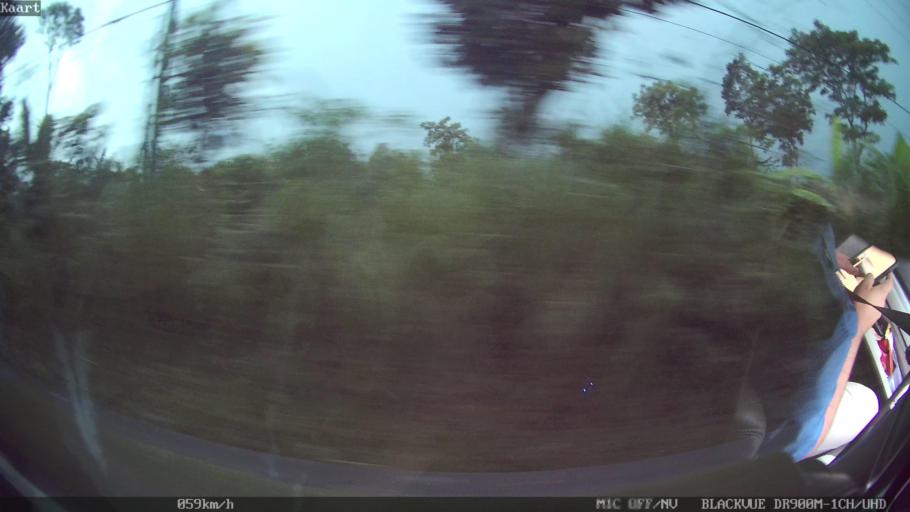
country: ID
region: Bali
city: Banjar Kedisan
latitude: -8.2842
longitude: 115.3206
